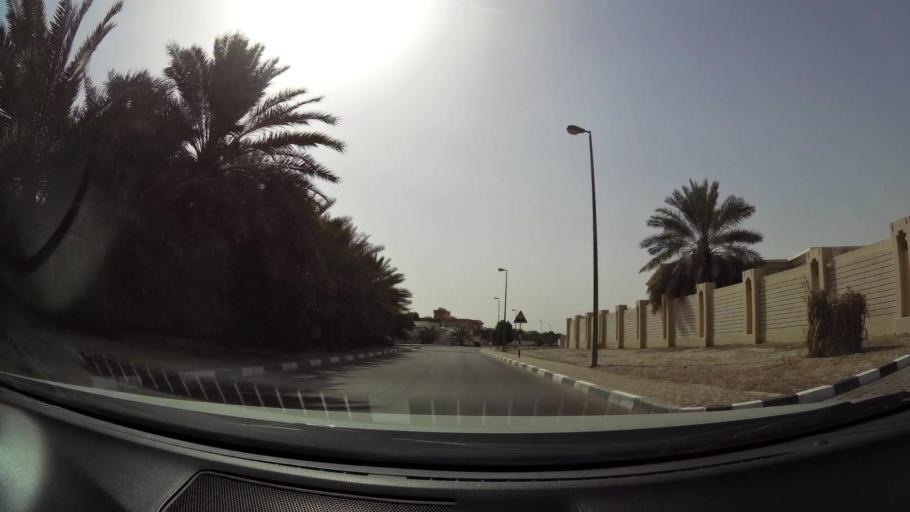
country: AE
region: Abu Dhabi
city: Al Ain
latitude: 24.2454
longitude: 55.6952
